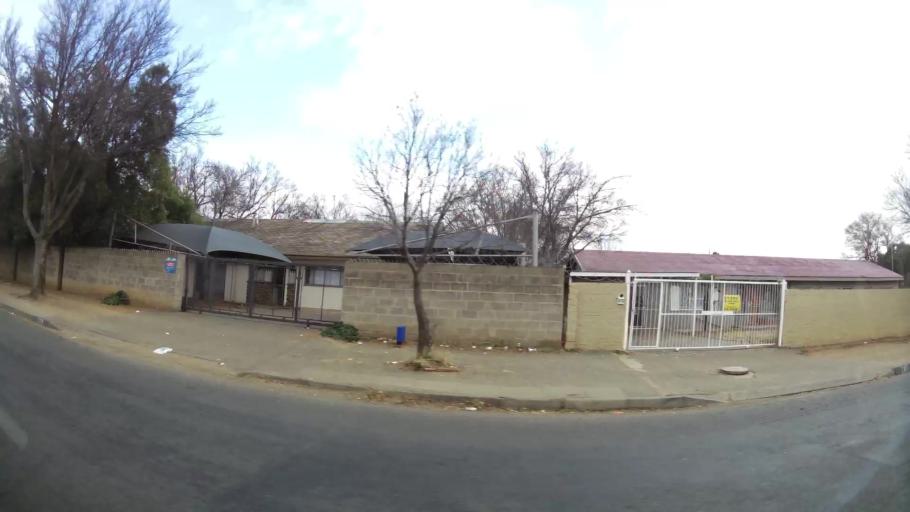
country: ZA
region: Orange Free State
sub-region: Mangaung Metropolitan Municipality
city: Bloemfontein
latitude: -29.1190
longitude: 26.1944
